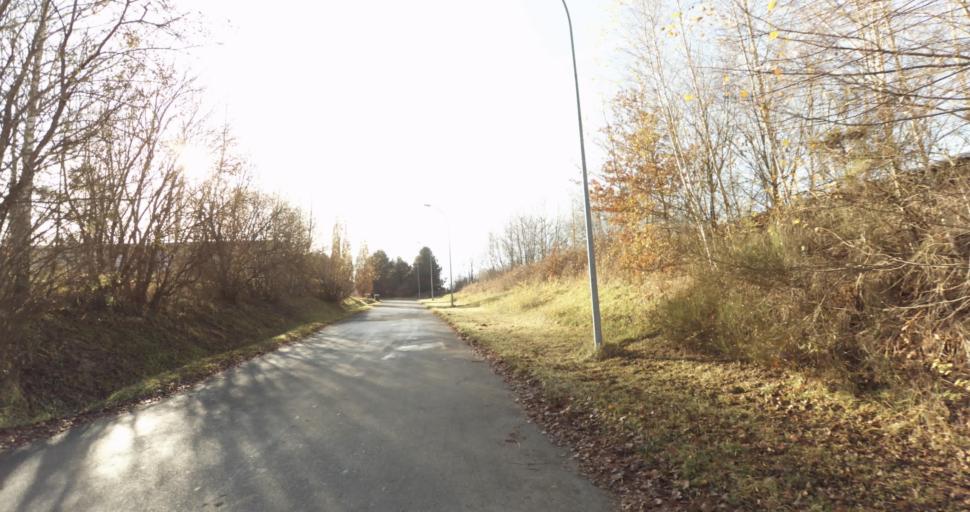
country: FR
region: Limousin
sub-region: Departement de la Haute-Vienne
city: Saint-Priest-sous-Aixe
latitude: 45.8035
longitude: 1.1168
